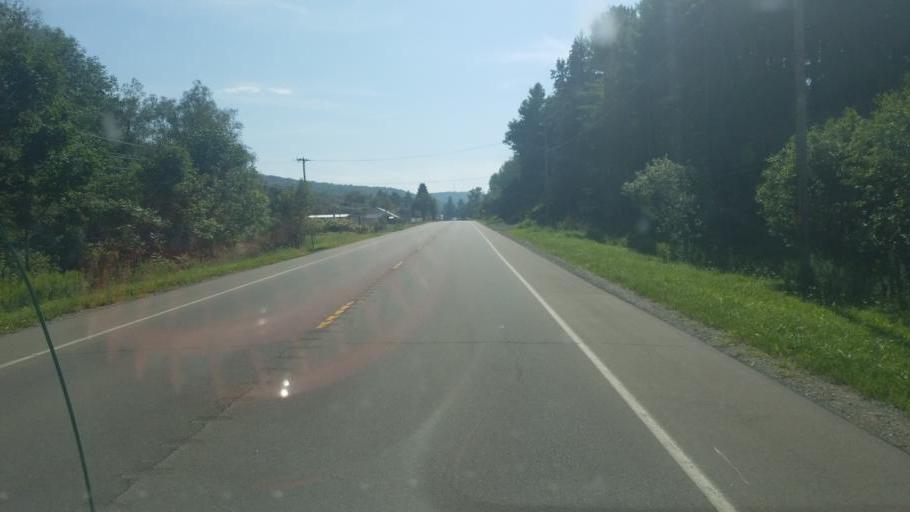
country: US
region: New York
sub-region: Allegany County
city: Wellsville
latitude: 42.0910
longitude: -78.0568
